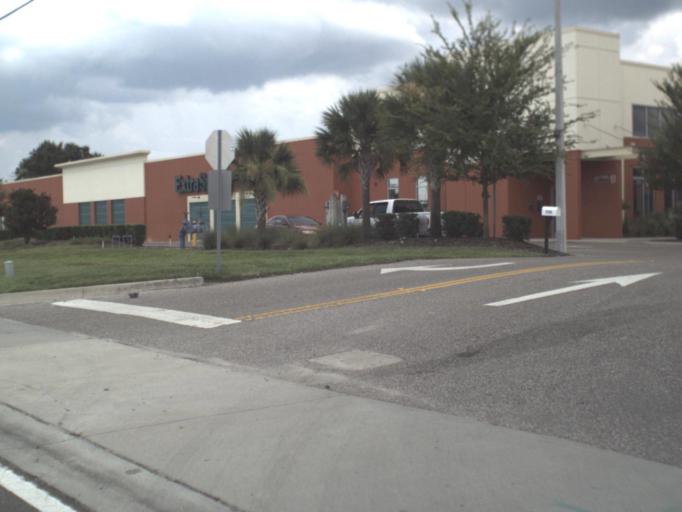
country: US
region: Florida
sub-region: Pasco County
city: Land O' Lakes
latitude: 28.1945
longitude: -82.4650
